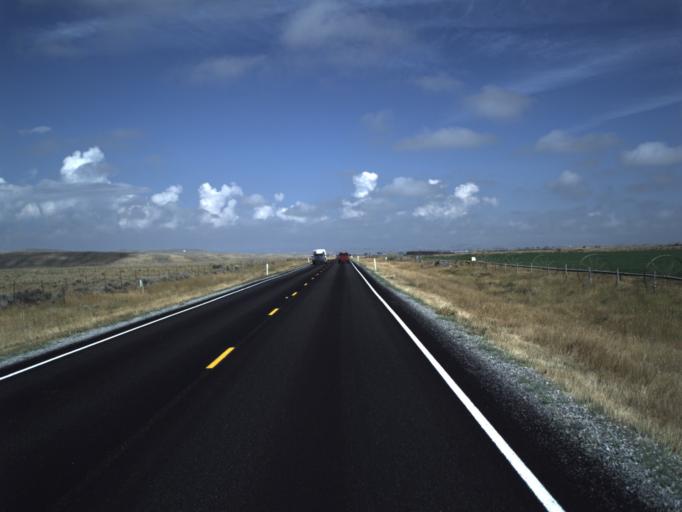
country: US
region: Utah
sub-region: Rich County
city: Randolph
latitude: 41.5628
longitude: -111.1579
